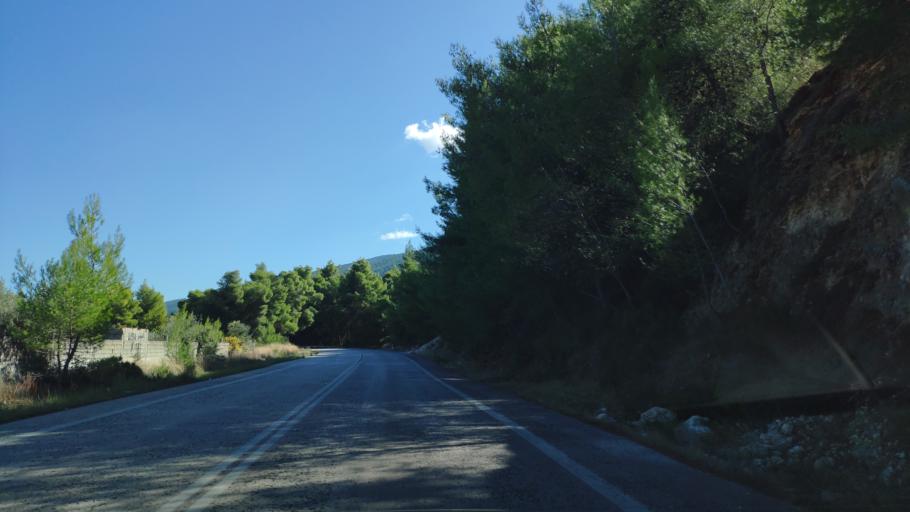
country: GR
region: Peloponnese
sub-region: Nomos Korinthias
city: Loutra Oraias Elenis
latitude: 37.8341
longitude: 23.0224
